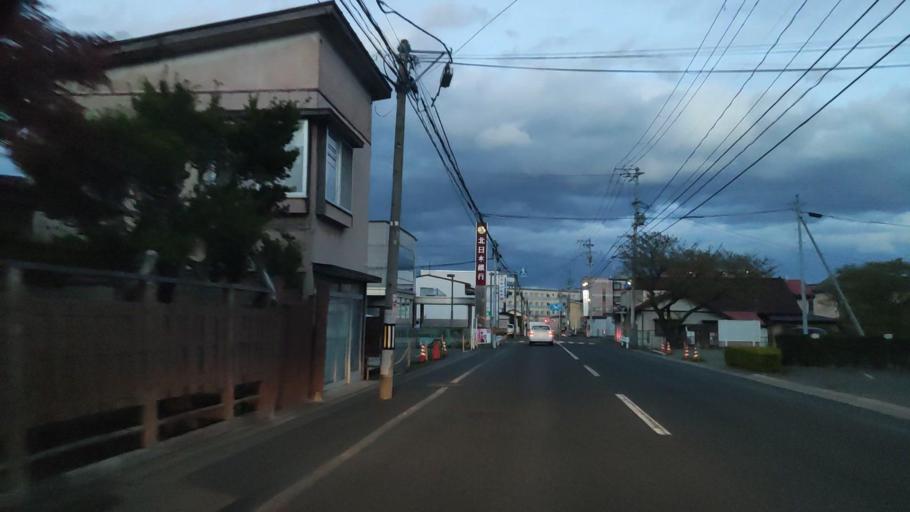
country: JP
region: Iwate
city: Morioka-shi
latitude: 39.7157
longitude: 141.1265
